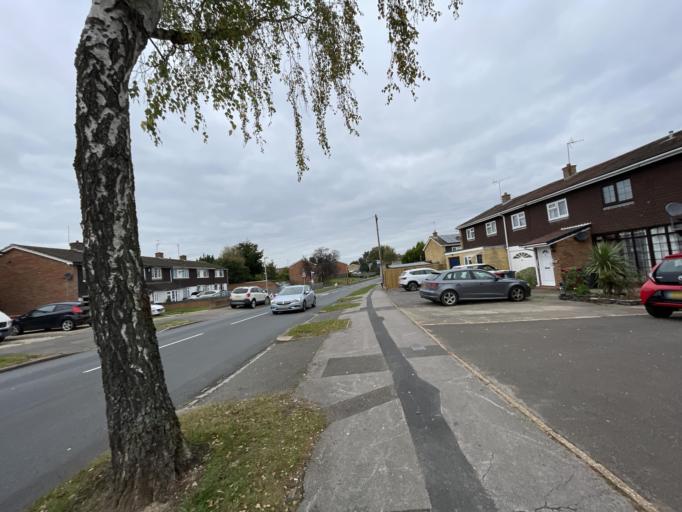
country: GB
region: England
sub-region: West Berkshire
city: Tilehurst
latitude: 51.4550
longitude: -1.0360
